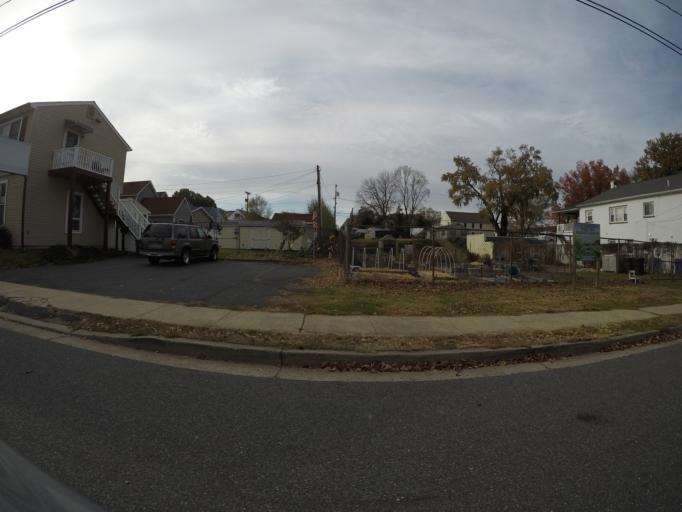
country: US
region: Maryland
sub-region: Harford County
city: Havre de Grace
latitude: 39.5470
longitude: -76.0880
